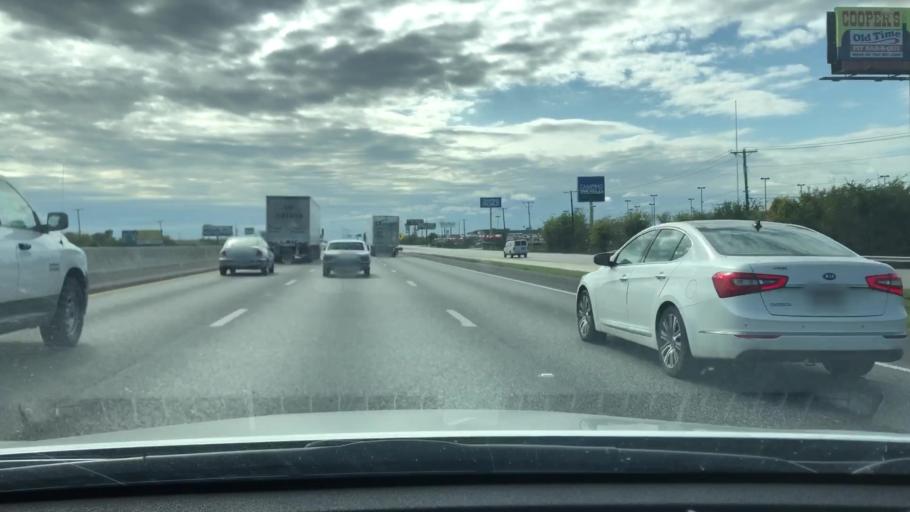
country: US
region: Texas
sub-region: Guadalupe County
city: Lake Dunlap
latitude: 29.7365
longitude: -98.0699
